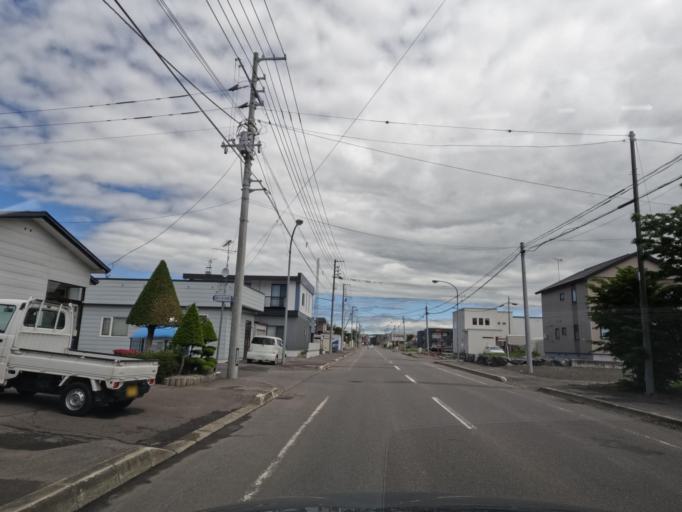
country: JP
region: Hokkaido
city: Shimo-furano
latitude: 43.4567
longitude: 142.4638
